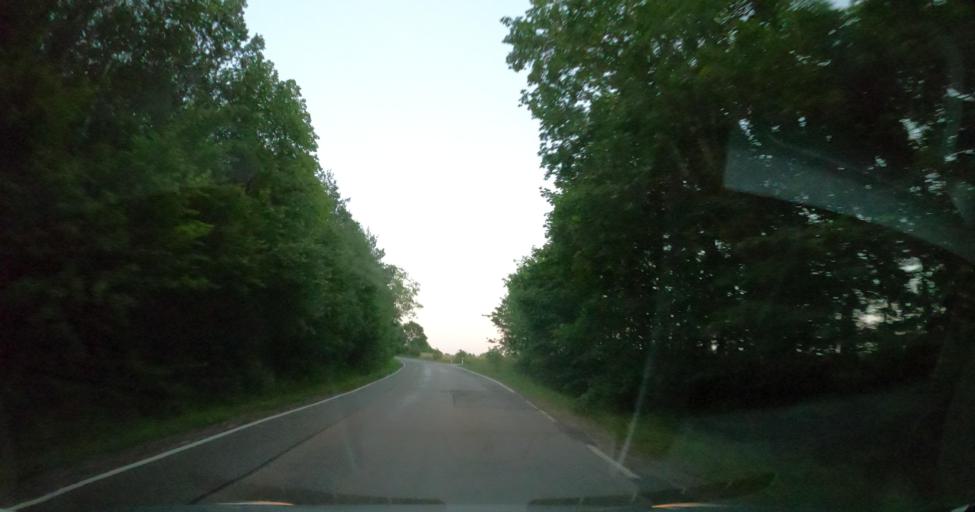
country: PL
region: Pomeranian Voivodeship
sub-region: Powiat wejherowski
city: Szemud
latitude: 54.4639
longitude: 18.1283
